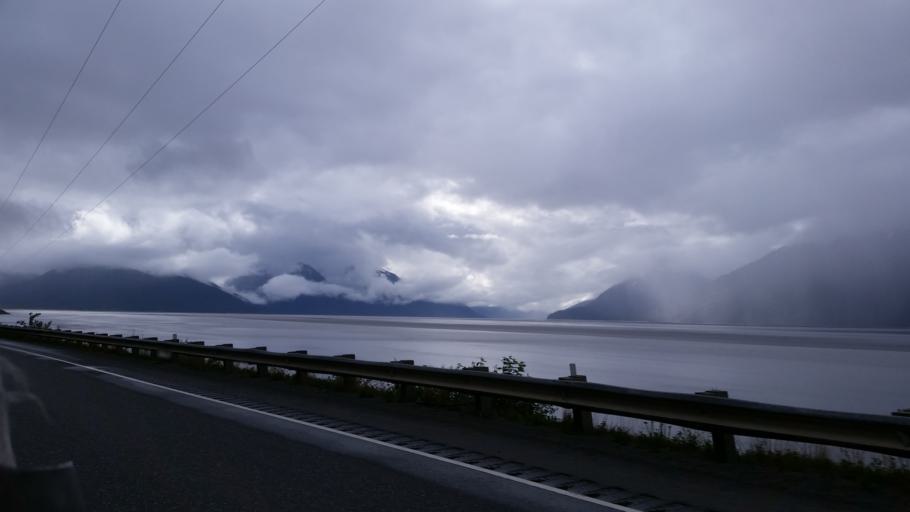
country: US
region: Alaska
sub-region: Anchorage Municipality
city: Girdwood
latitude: 60.9350
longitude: -149.3010
